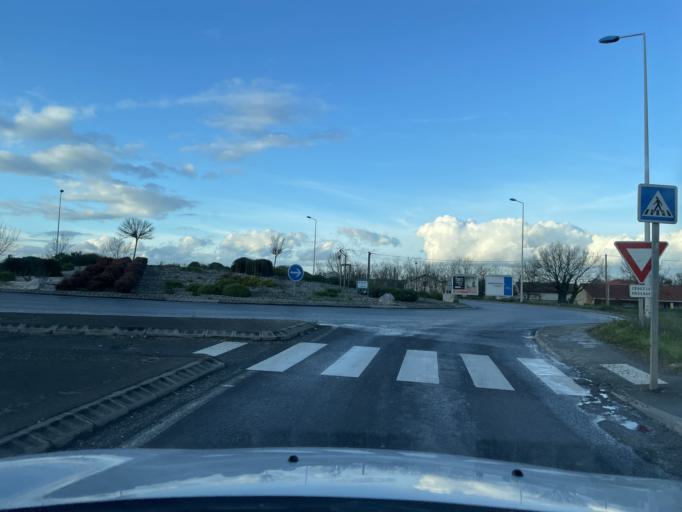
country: FR
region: Midi-Pyrenees
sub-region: Departement de la Haute-Garonne
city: Tournefeuille
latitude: 43.6045
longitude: 1.3072
